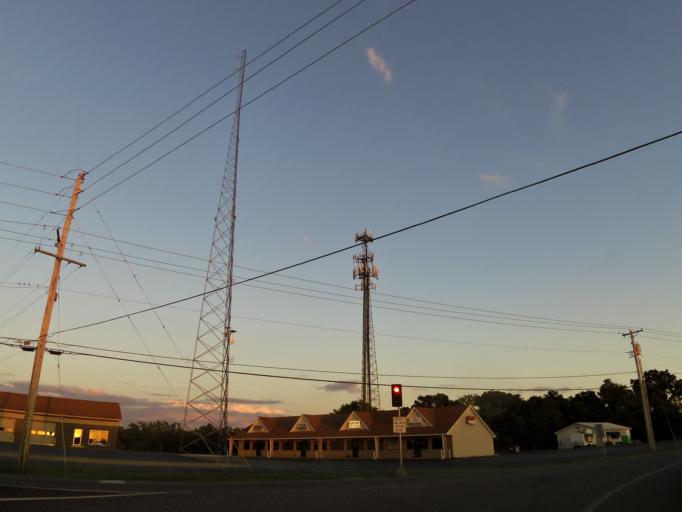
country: US
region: Missouri
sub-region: Jefferson County
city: Hillsboro
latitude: 38.2236
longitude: -90.5736
